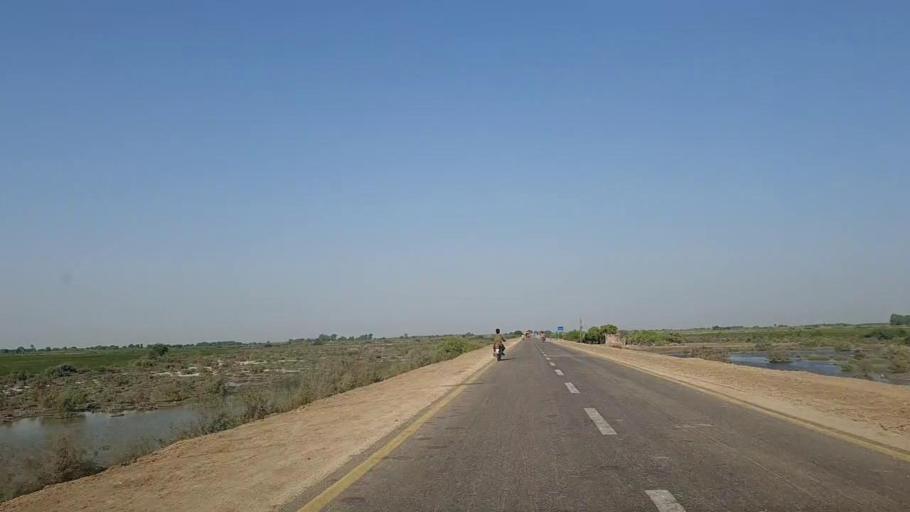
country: PK
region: Sindh
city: Jati
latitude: 24.4034
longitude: 68.2951
